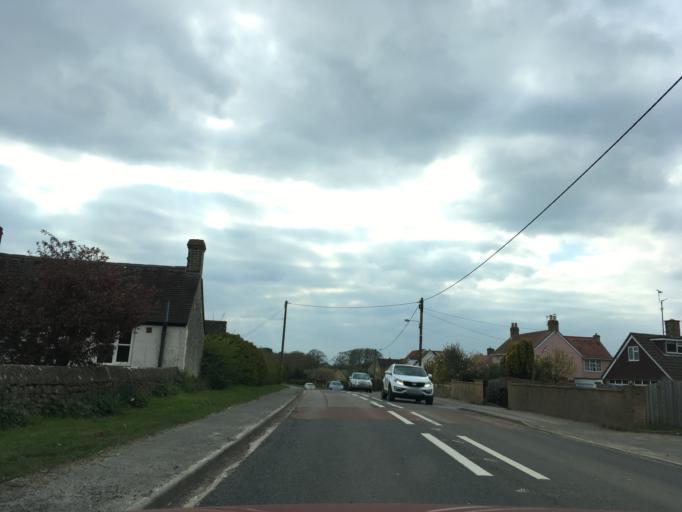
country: GB
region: England
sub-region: Oxfordshire
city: Stonesfield
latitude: 51.8248
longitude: -1.4004
